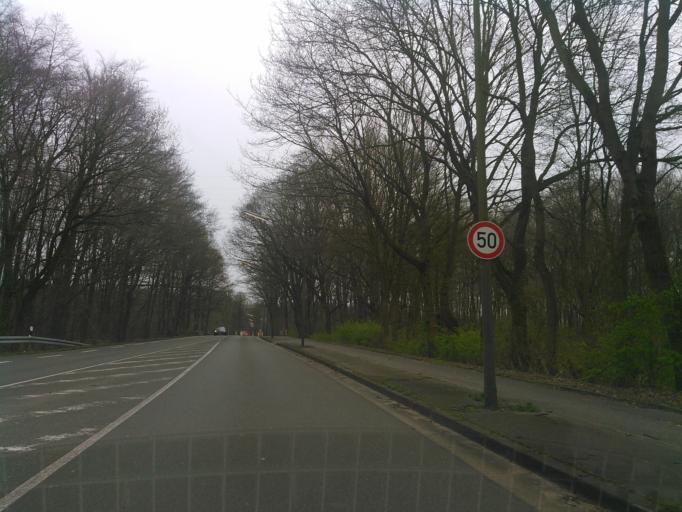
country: DE
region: North Rhine-Westphalia
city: Marl
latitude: 51.6718
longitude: 7.0765
